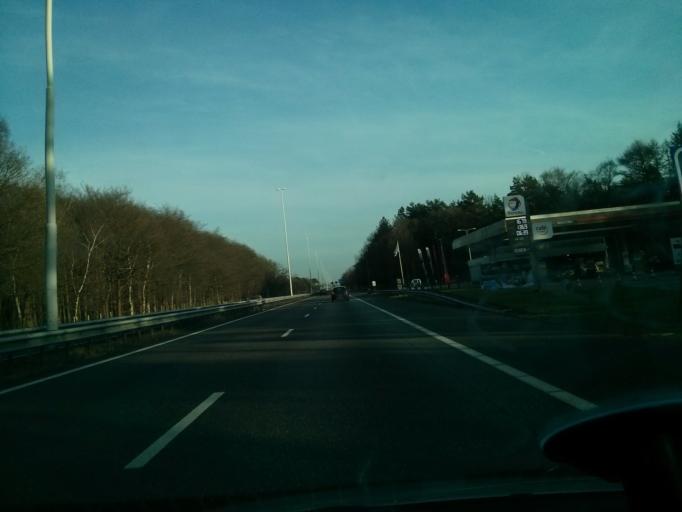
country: NL
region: North Brabant
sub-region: Gemeente Oisterwijk
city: Oisterwijk
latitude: 51.5431
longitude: 5.1573
